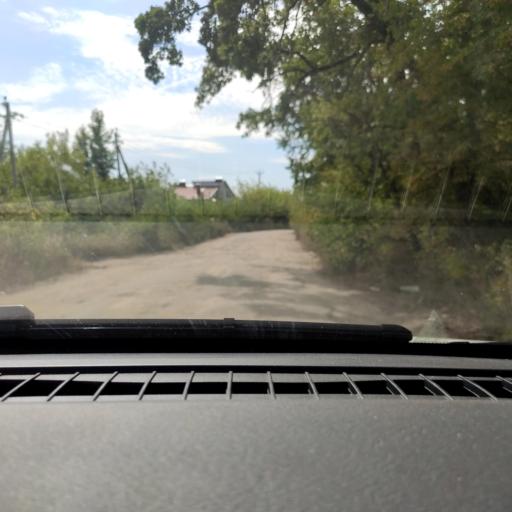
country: RU
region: Voronezj
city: Pridonskoy
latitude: 51.7444
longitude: 39.0731
